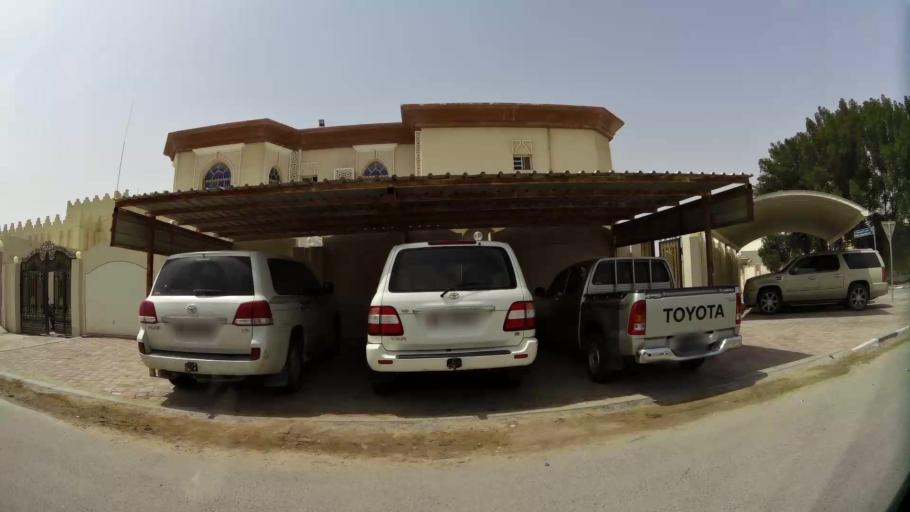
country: QA
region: Baladiyat ar Rayyan
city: Ar Rayyan
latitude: 25.2363
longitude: 51.4198
